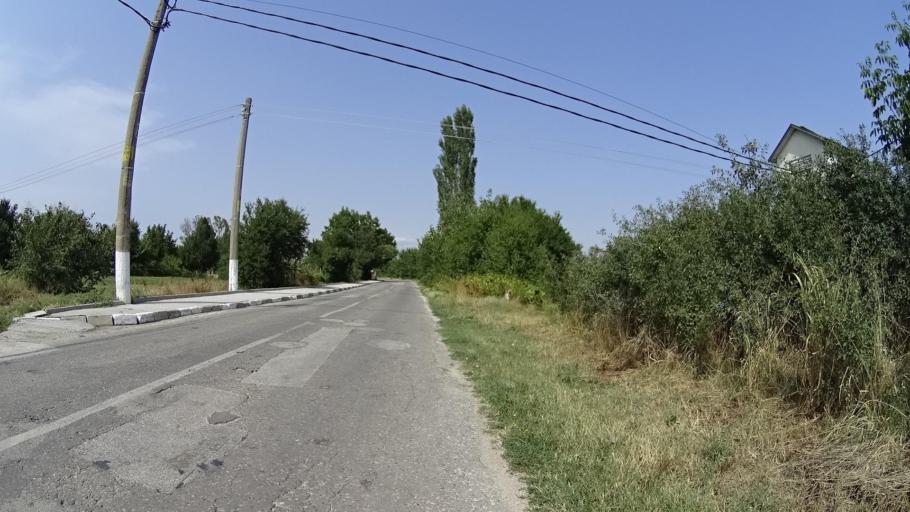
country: BG
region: Plovdiv
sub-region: Obshtina Plovdiv
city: Plovdiv
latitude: 42.2190
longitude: 24.7842
